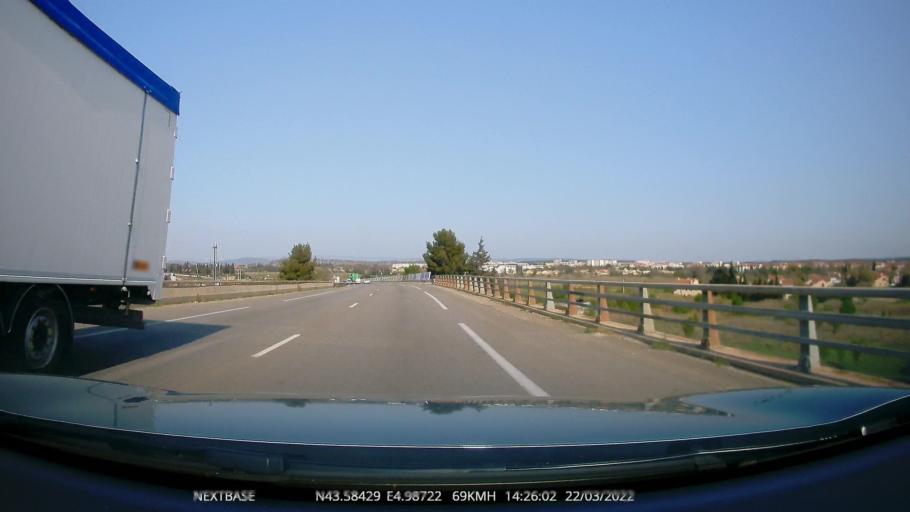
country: FR
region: Provence-Alpes-Cote d'Azur
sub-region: Departement des Bouches-du-Rhone
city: Miramas
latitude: 43.5845
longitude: 4.9875
